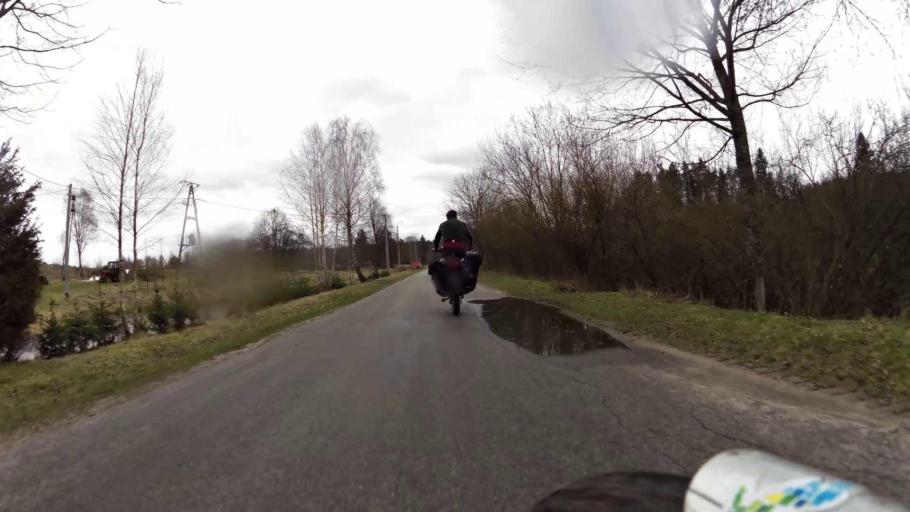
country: PL
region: Pomeranian Voivodeship
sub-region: Powiat bytowski
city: Trzebielino
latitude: 54.0800
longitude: 17.1181
